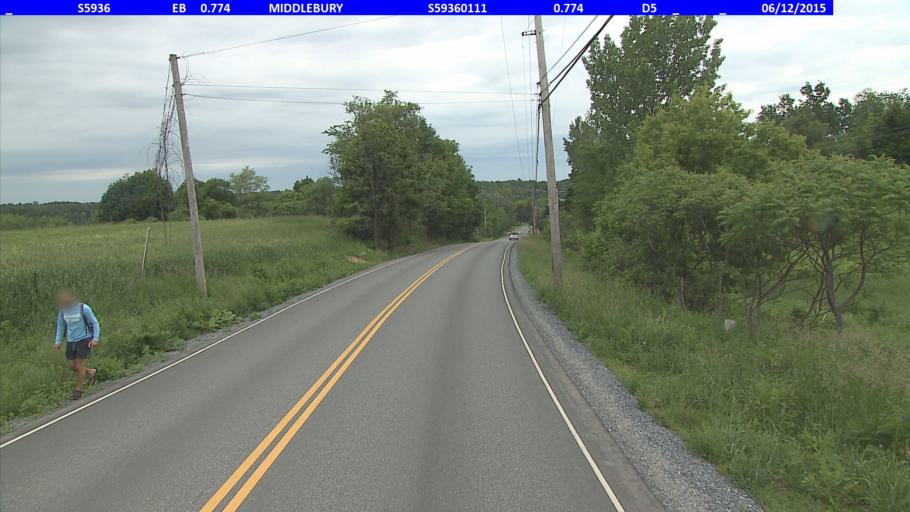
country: US
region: Vermont
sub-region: Addison County
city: Middlebury (village)
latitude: 44.0239
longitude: -73.1500
